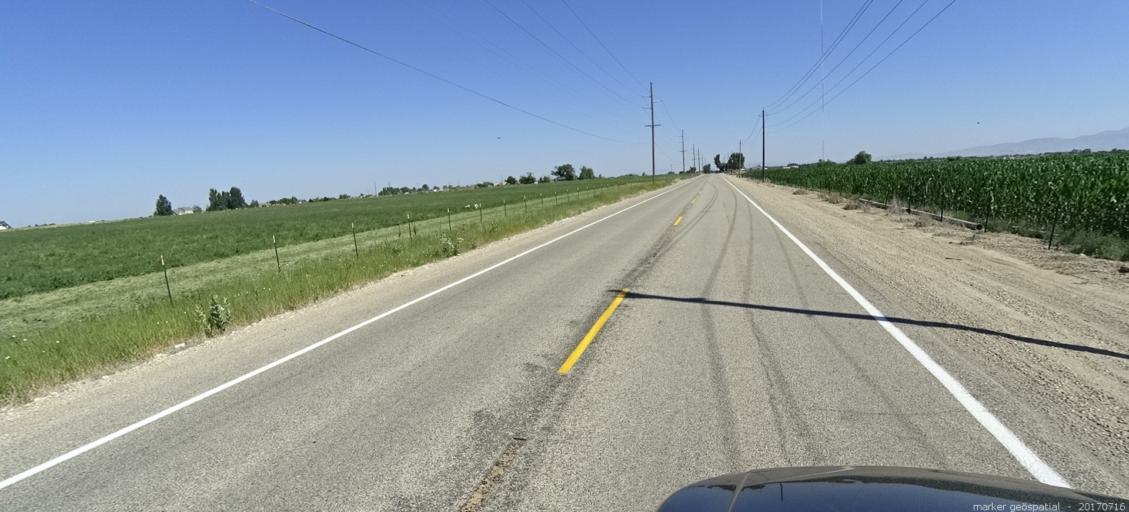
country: US
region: Idaho
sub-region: Ada County
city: Kuna
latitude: 43.5123
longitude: -116.3345
